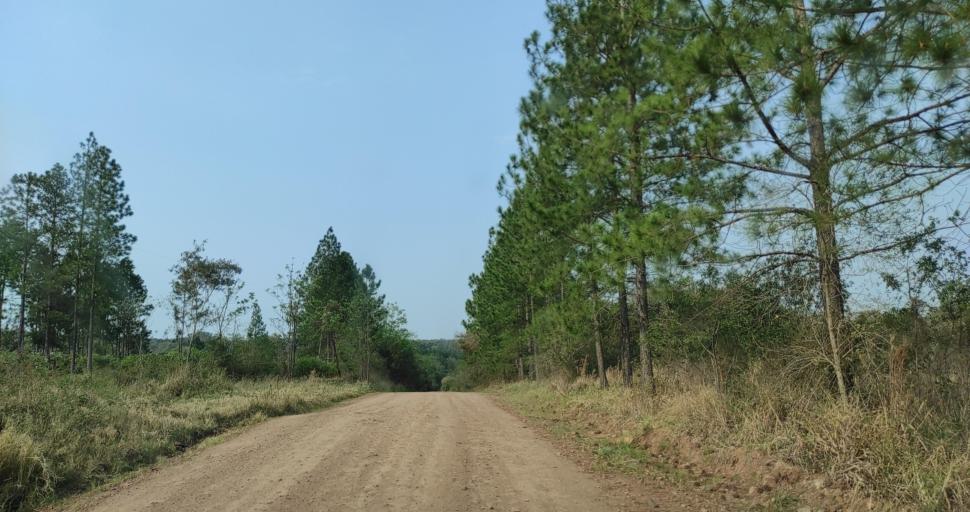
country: AR
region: Misiones
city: Cerro Azul
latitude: -27.6263
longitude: -55.5414
